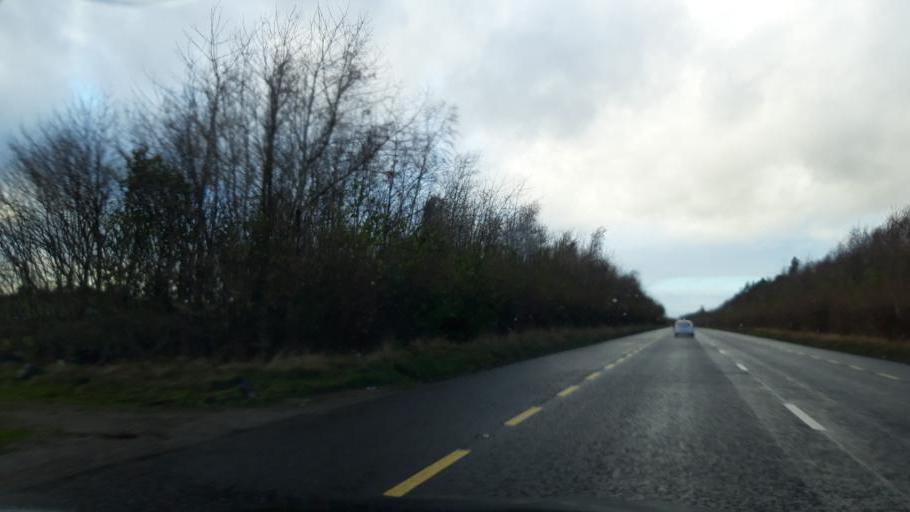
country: IE
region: Leinster
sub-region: Lu
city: Ardee
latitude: 53.8977
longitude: -6.5893
